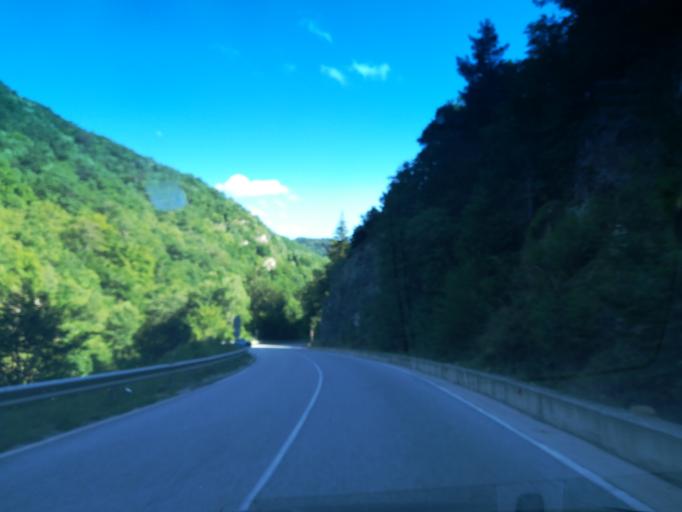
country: BG
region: Smolyan
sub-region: Obshtina Chepelare
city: Chepelare
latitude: 41.7903
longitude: 24.7086
